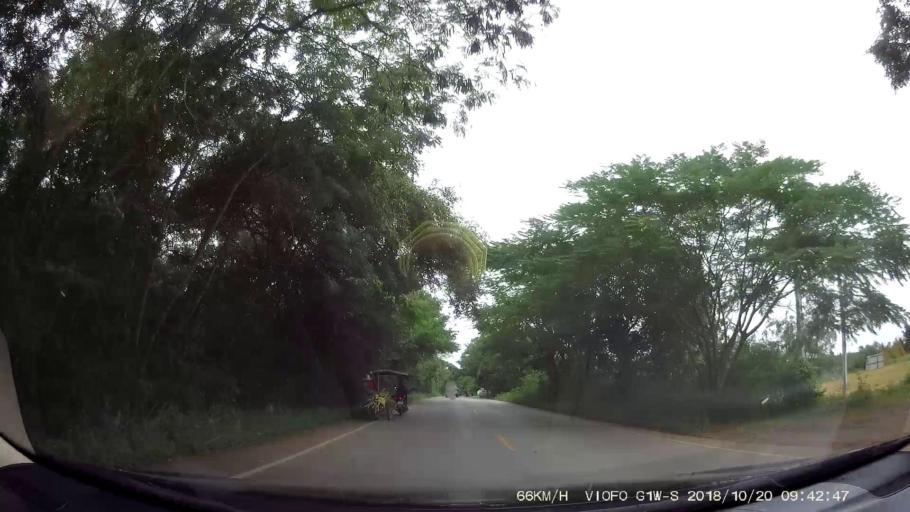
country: TH
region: Chaiyaphum
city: Khon San
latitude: 16.4672
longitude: 101.9509
